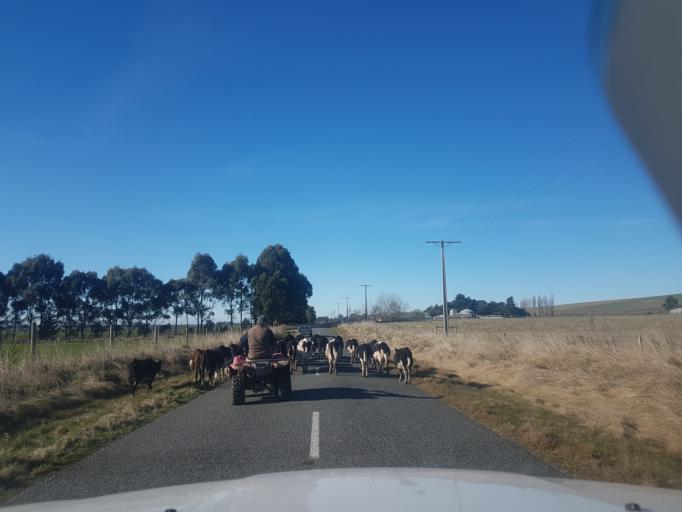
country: NZ
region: Canterbury
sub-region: Timaru District
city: Pleasant Point
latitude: -44.2910
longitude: 171.0626
